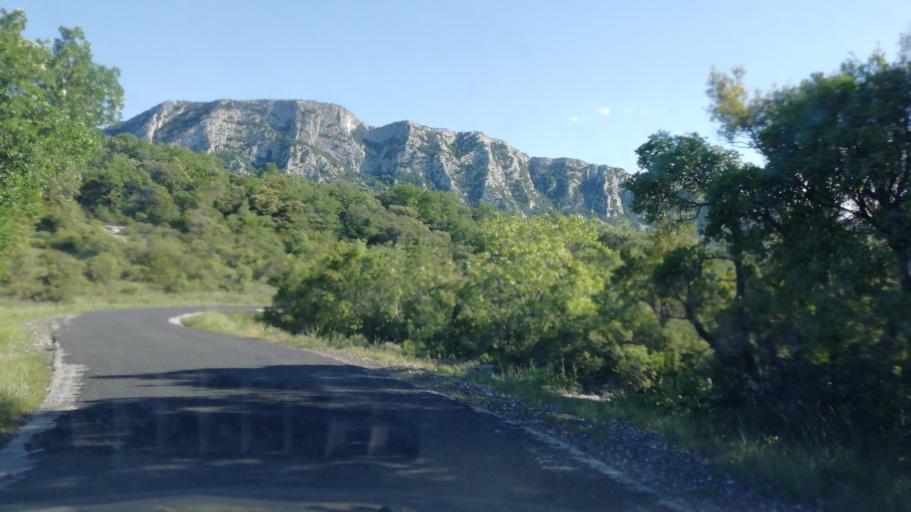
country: FR
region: Languedoc-Roussillon
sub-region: Departement de l'Herault
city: Saint-Mathieu-de-Treviers
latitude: 43.7920
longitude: 3.8086
